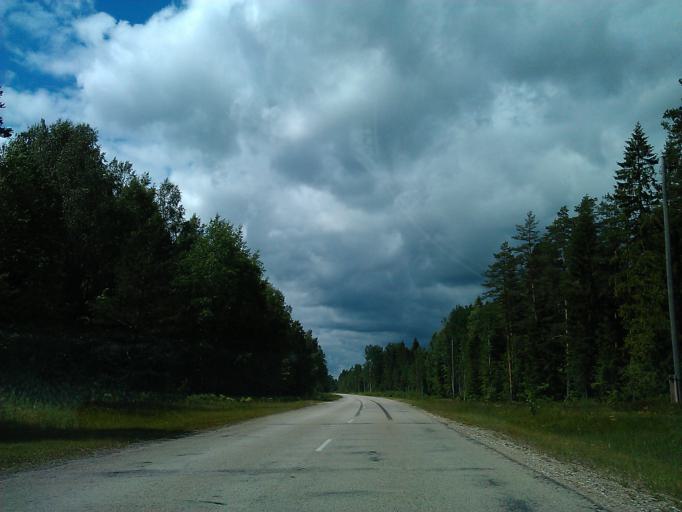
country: LV
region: Talsu Rajons
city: Stende
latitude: 57.0869
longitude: 22.5071
